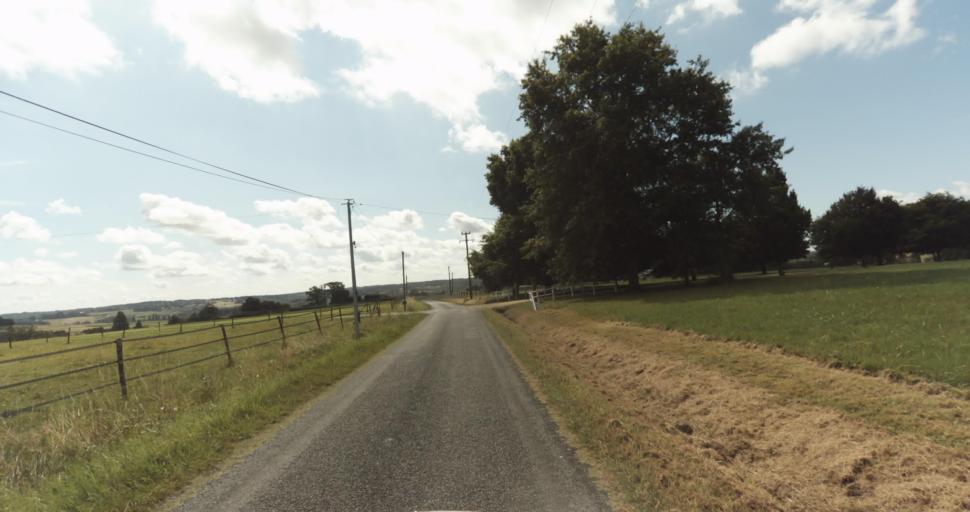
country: FR
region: Aquitaine
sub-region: Departement de la Gironde
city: Bazas
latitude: 44.4534
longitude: -0.1871
